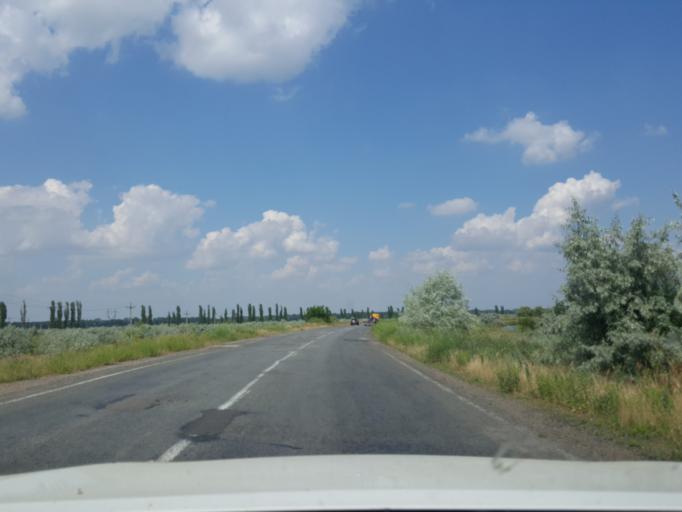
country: UA
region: Odessa
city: Bilyayivka
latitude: 46.4094
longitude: 30.1086
